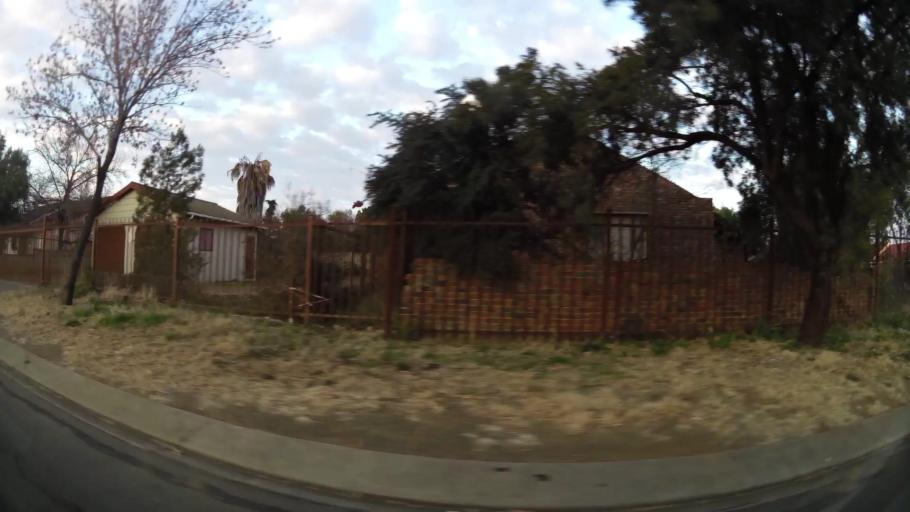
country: ZA
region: Orange Free State
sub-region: Mangaung Metropolitan Municipality
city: Bloemfontein
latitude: -29.1644
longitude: 26.1848
